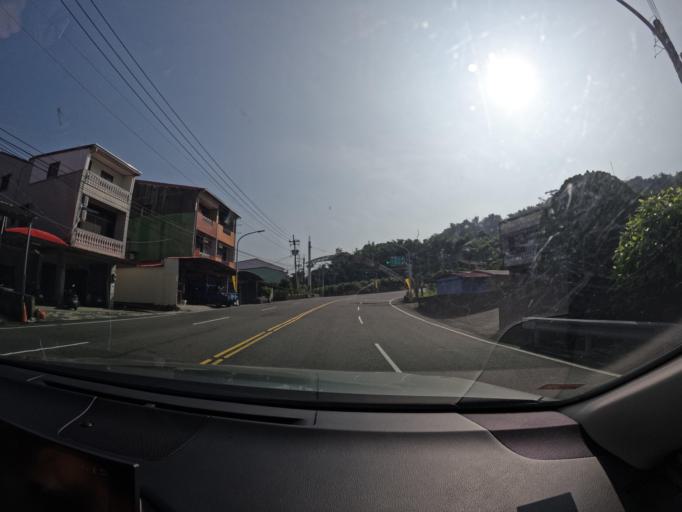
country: TW
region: Taiwan
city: Yujing
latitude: 23.0848
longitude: 120.5267
